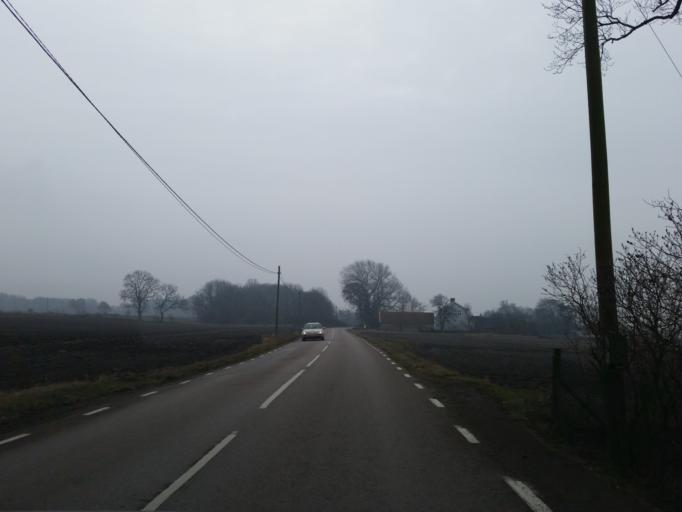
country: SE
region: Kalmar
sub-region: Morbylanga Kommun
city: Moerbylanga
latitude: 56.4204
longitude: 16.4134
